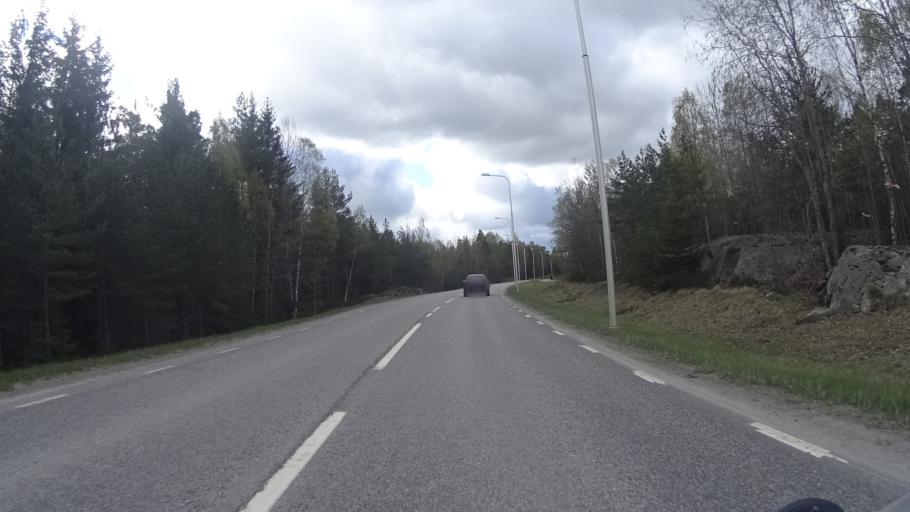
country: SE
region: Stockholm
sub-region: Botkyrka Kommun
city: Tullinge
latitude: 59.1990
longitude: 17.9287
